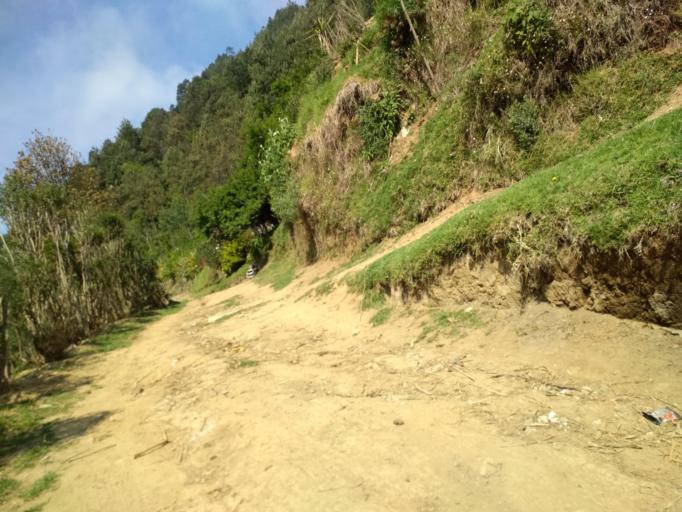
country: MX
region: Veracruz
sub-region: Mariano Escobedo
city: San Isidro el Berro
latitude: 18.9417
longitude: -97.2192
